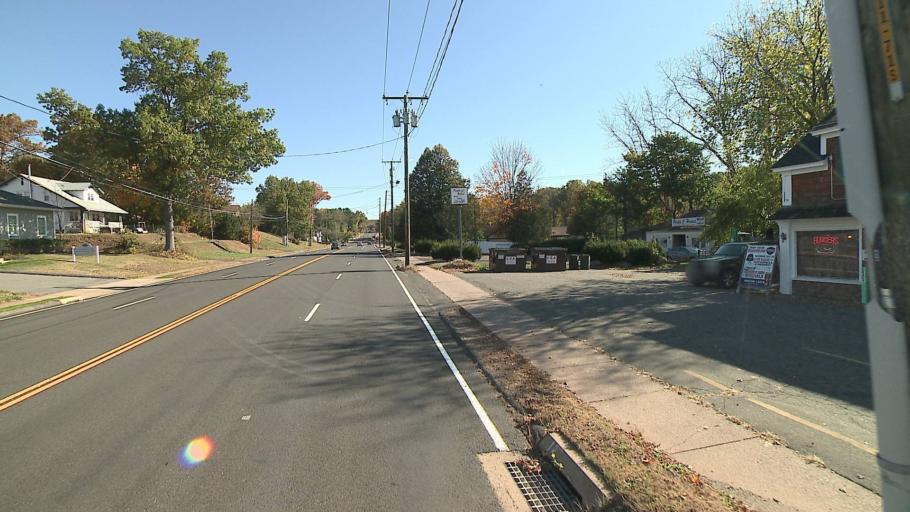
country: US
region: Connecticut
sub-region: Hartford County
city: Manchester
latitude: 41.7853
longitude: -72.4943
